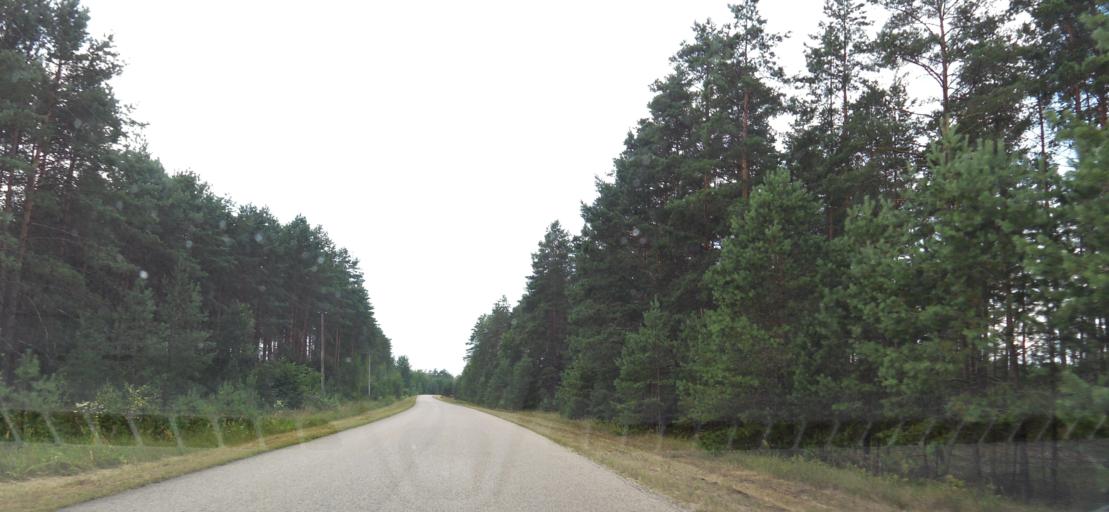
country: LT
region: Alytaus apskritis
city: Druskininkai
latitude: 53.9849
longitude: 24.2323
